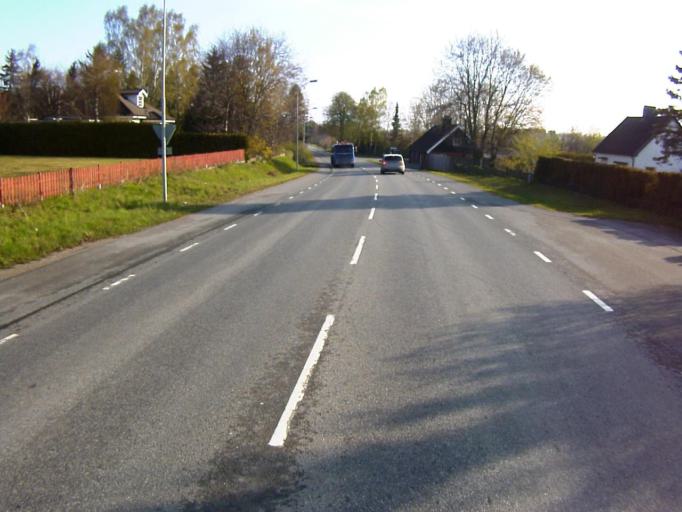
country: SE
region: Skane
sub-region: Kristianstads Kommun
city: Norra Asum
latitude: 56.0043
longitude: 14.0969
